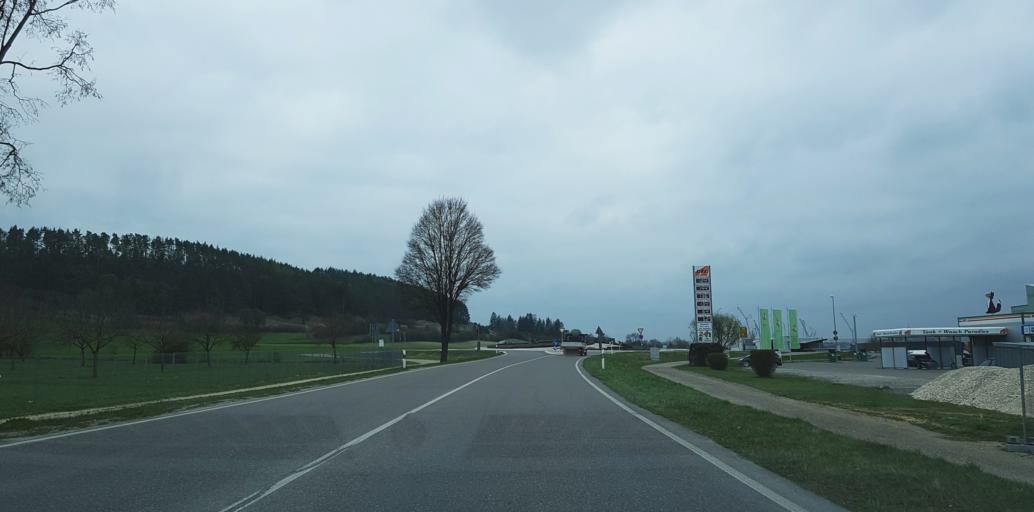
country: DE
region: Baden-Wuerttemberg
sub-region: Tuebingen Region
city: Allmendingen
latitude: 48.3231
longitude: 9.7296
